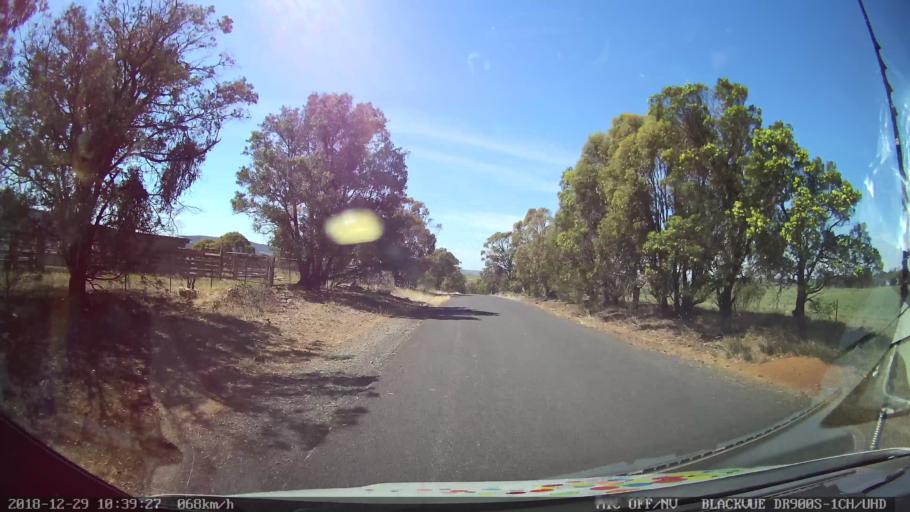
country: AU
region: New South Wales
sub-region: Palerang
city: Bungendore
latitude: -35.0068
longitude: 149.5105
